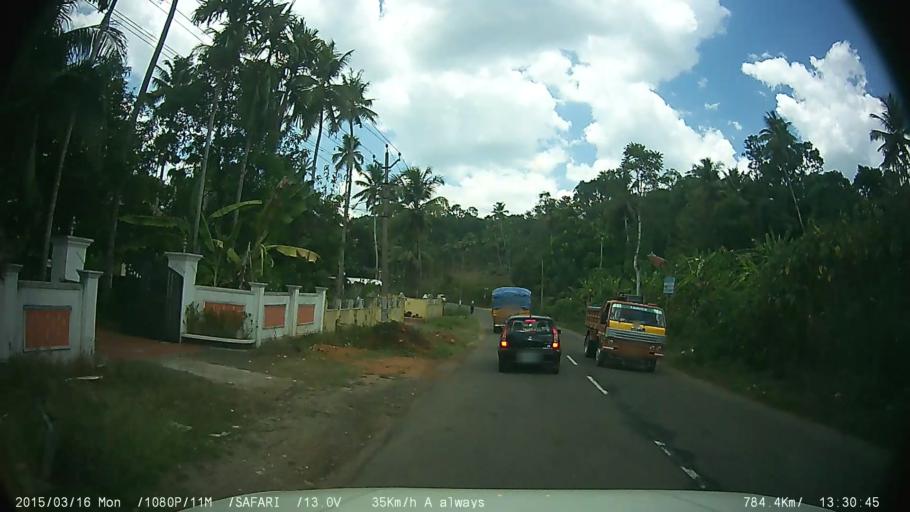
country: IN
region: Kerala
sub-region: Ernakulam
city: Muvattupuzha
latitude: 9.8928
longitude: 76.5892
